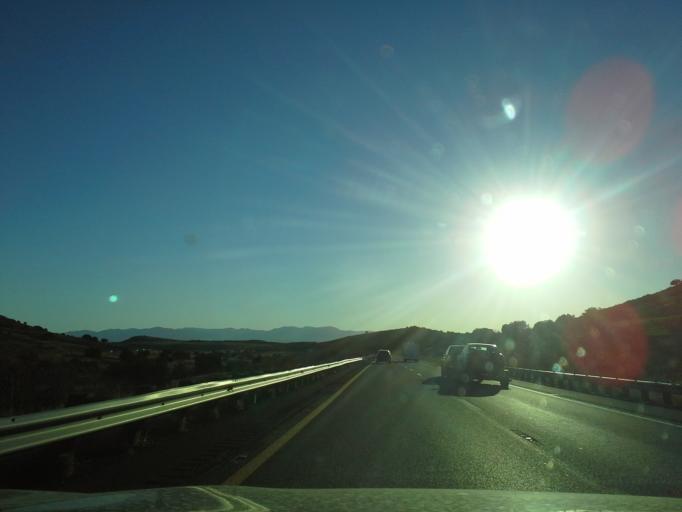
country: US
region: Arizona
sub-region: Yavapai County
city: Camp Verde
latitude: 34.4861
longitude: -112.0138
